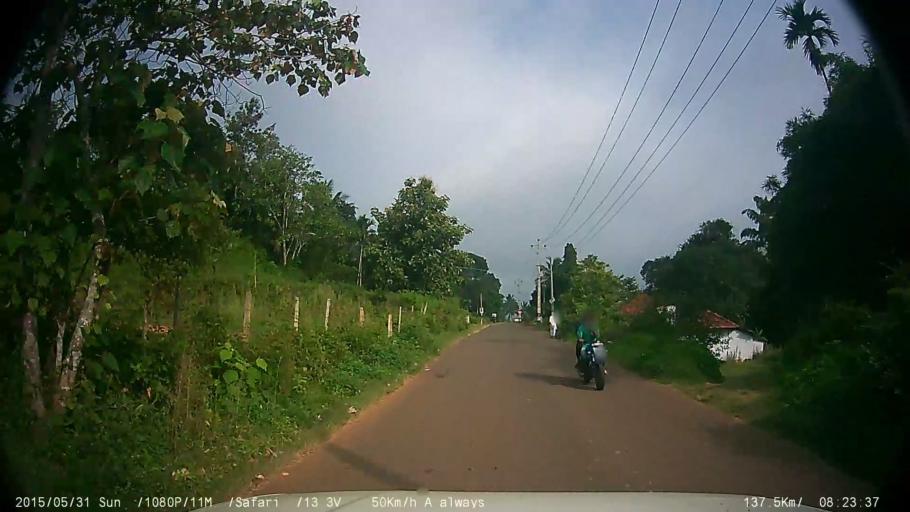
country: IN
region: Kerala
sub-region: Wayanad
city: Kalpetta
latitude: 11.6737
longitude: 75.9688
